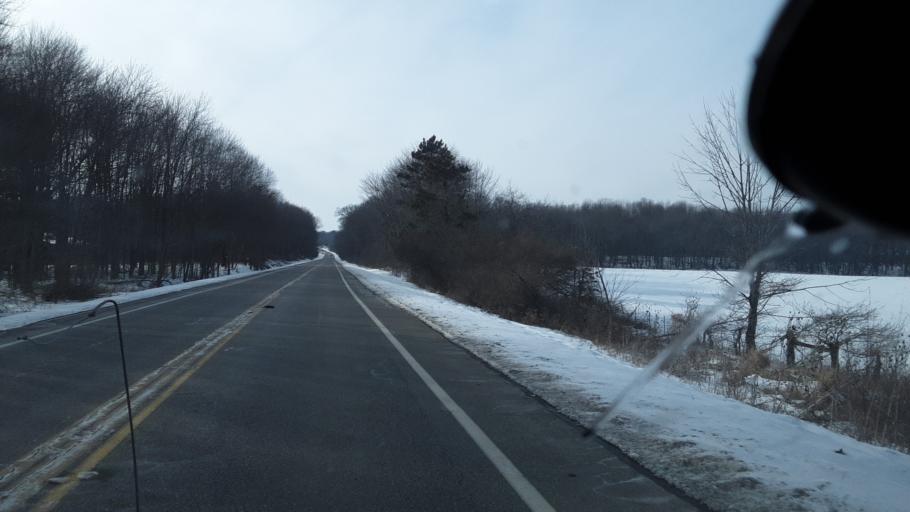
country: US
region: Ohio
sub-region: Stark County
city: Hartville
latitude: 41.0269
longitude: -81.3331
